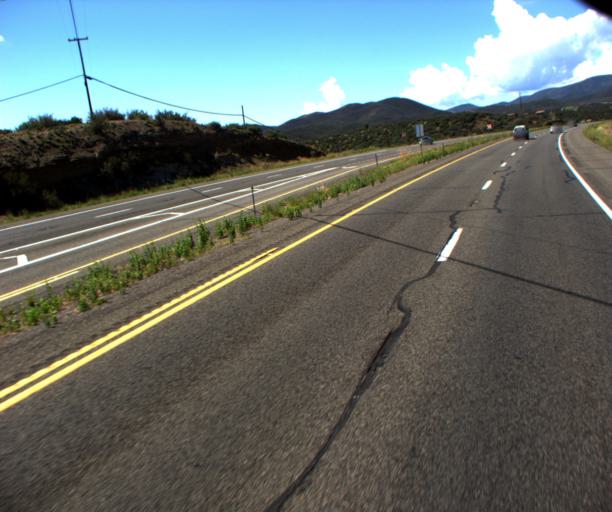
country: US
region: Arizona
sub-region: Yavapai County
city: Dewey-Humboldt
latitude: 34.4876
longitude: -112.2520
